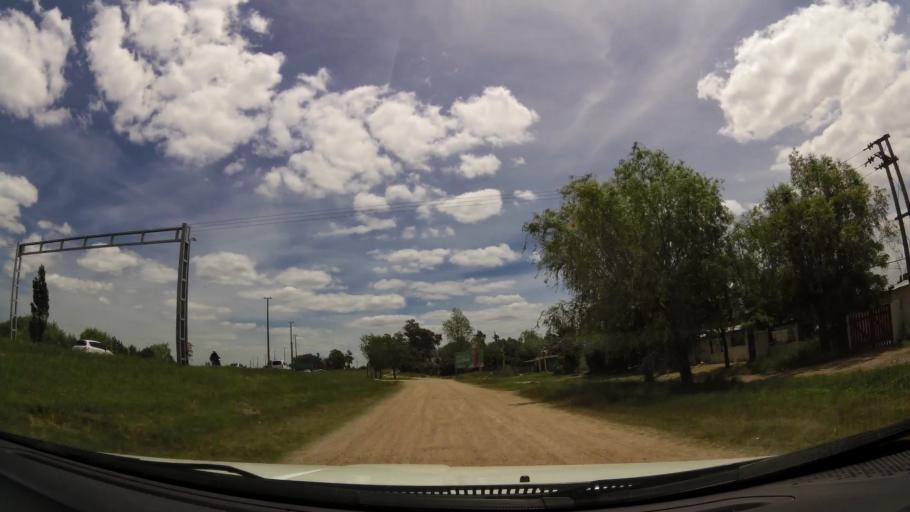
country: UY
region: Montevideo
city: Montevideo
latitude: -34.8658
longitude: -56.2473
